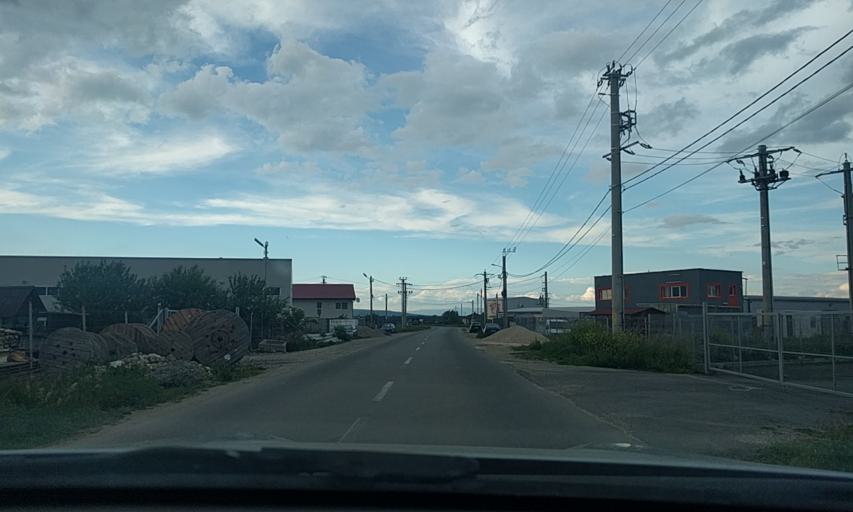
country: RO
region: Brasov
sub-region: Comuna Harman
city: Harman
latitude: 45.7240
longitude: 25.6975
